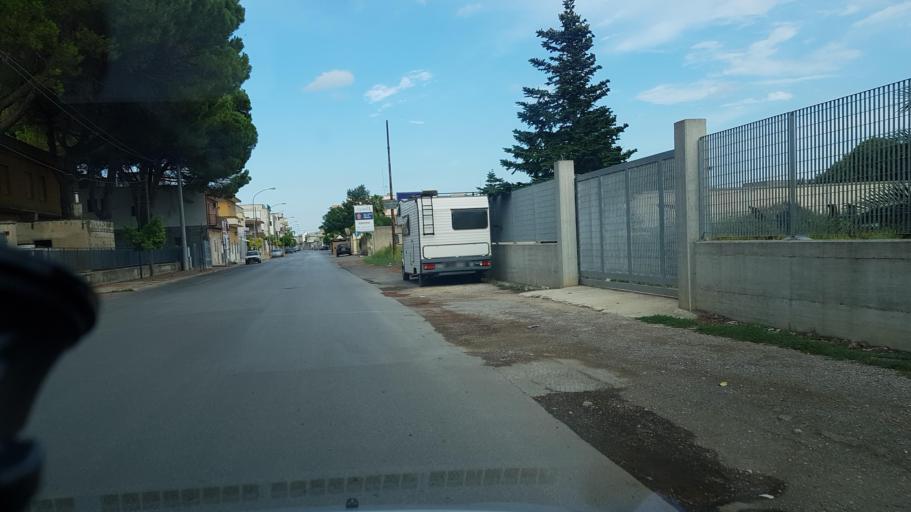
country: IT
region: Apulia
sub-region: Provincia di Brindisi
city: Latiano
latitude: 40.5493
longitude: 17.7094
